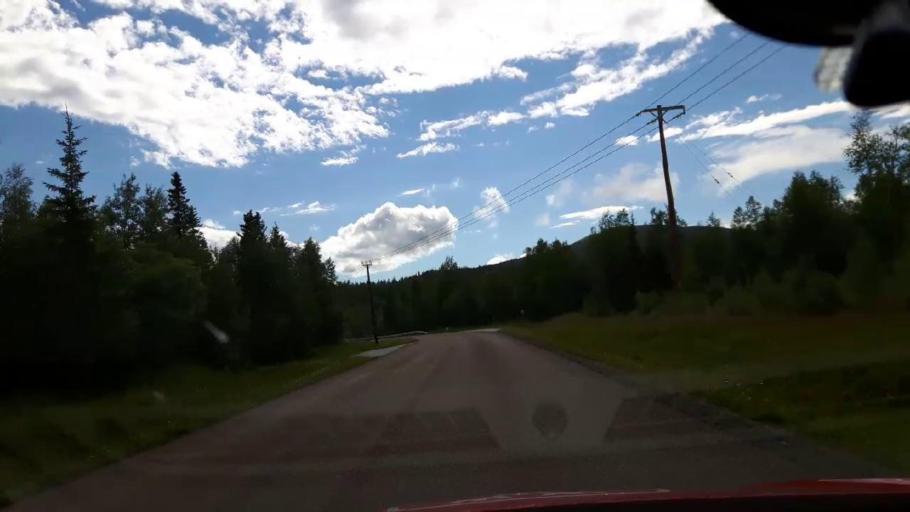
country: SE
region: Jaemtland
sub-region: Are Kommun
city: Are
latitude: 63.3050
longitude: 13.2233
